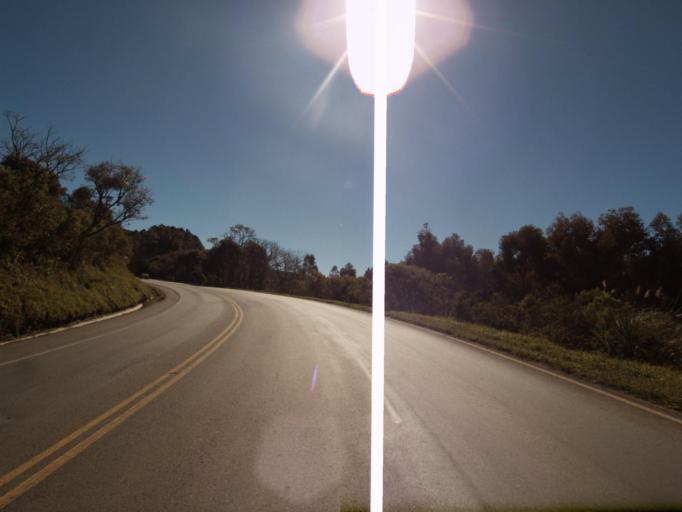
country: BR
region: Santa Catarina
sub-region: Joacaba
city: Joacaba
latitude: -26.9920
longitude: -51.7519
